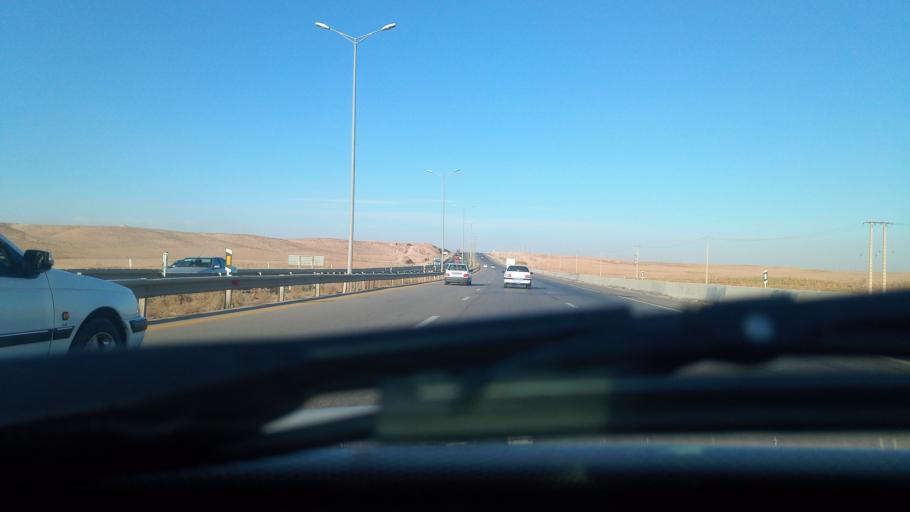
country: IR
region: Razavi Khorasan
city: Mashhad
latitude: 36.0609
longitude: 59.7233
